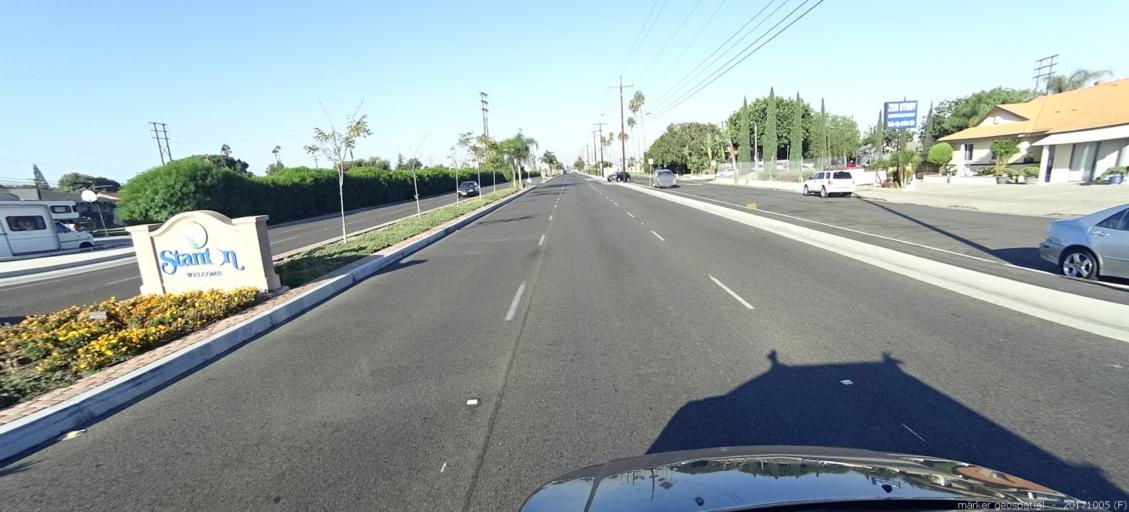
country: US
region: California
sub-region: Orange County
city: Stanton
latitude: 33.8031
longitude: -117.9784
